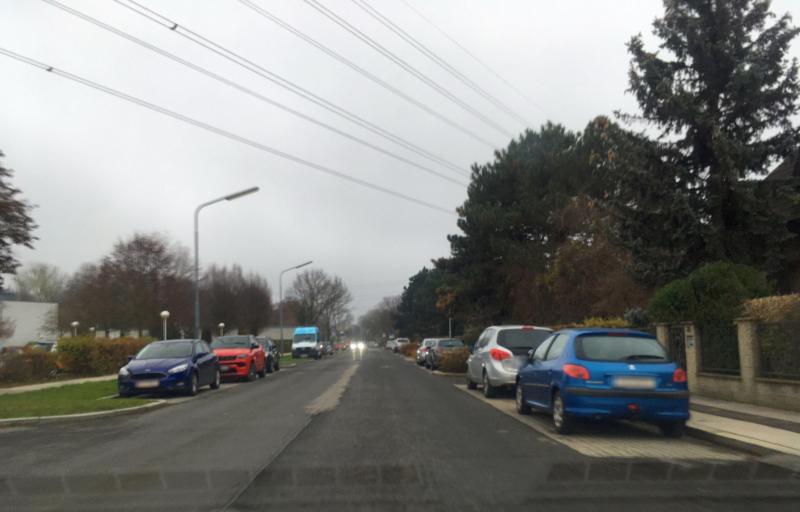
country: AT
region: Lower Austria
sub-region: Politischer Bezirk Wien-Umgebung
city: Gerasdorf bei Wien
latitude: 48.2149
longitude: 16.4695
